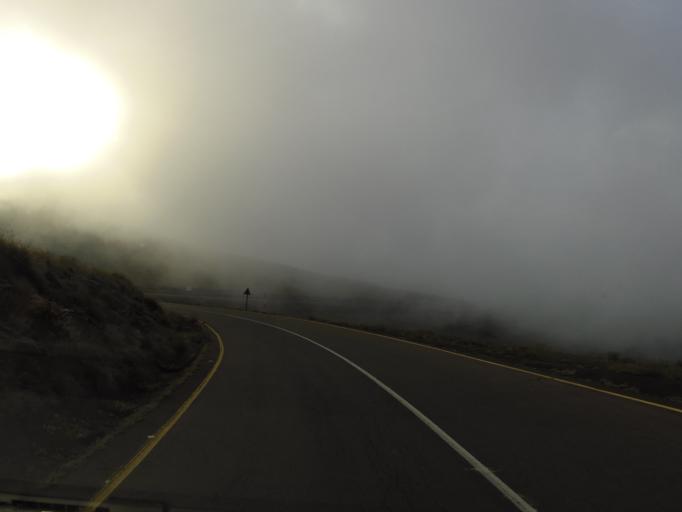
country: LS
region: Butha-Buthe
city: Butha-Buthe
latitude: -29.0682
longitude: 28.4093
